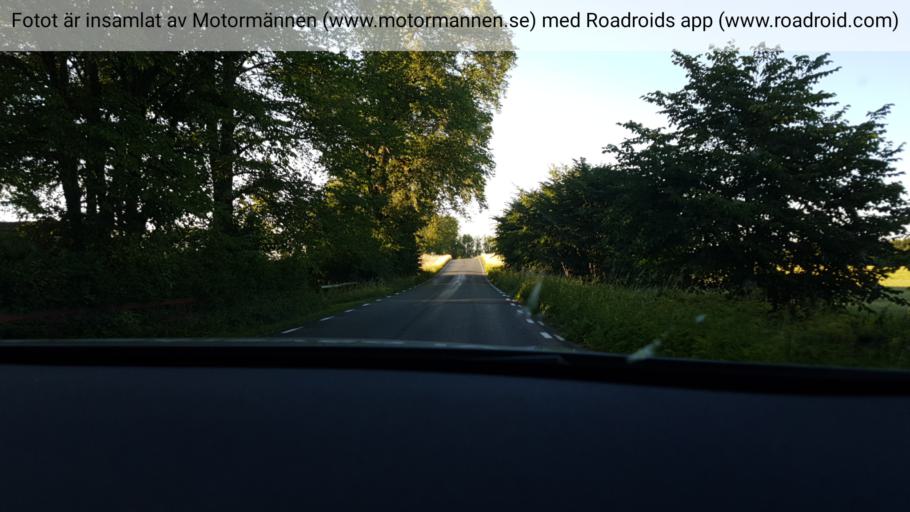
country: SE
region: Vaestra Goetaland
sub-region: Skovde Kommun
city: Skultorp
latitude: 58.2571
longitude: 13.7895
